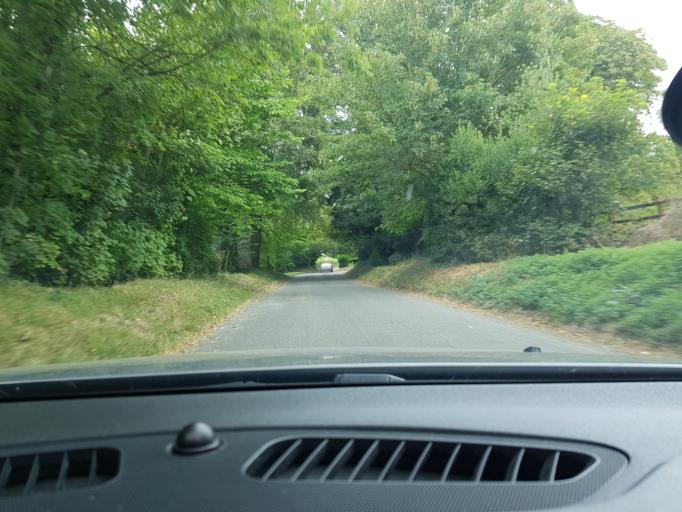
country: GB
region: England
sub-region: West Berkshire
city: Farnborough
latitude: 51.5126
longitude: -1.4077
